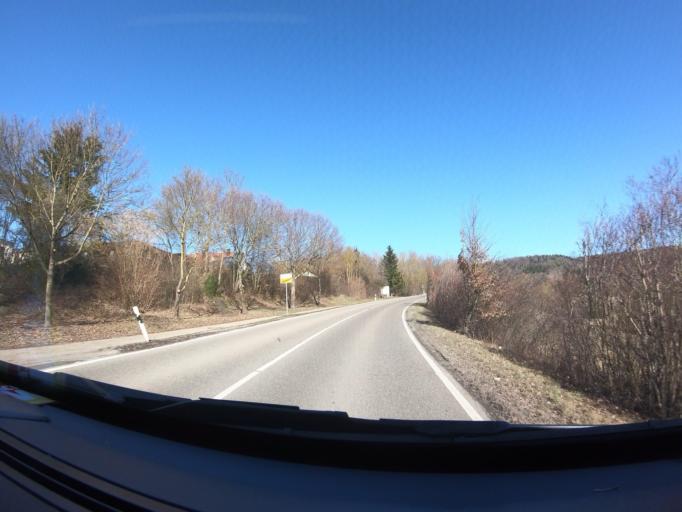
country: DE
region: Baden-Wuerttemberg
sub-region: Regierungsbezirk Stuttgart
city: Gaildorf
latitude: 49.0081
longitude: 9.7764
